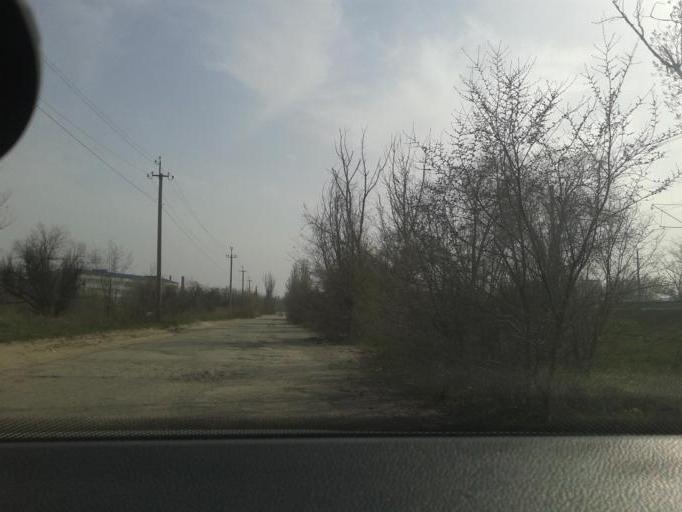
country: RU
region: Volgograd
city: Volgograd
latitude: 48.6356
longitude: 44.4391
